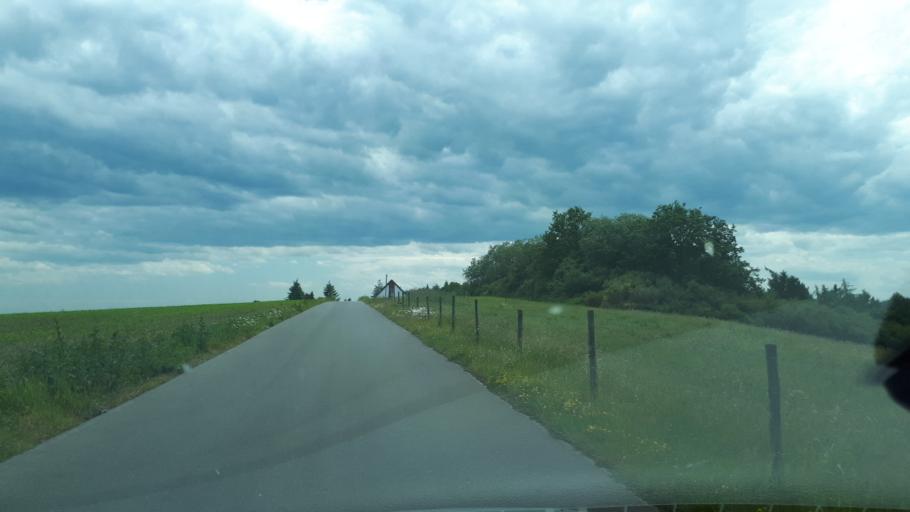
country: DE
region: Rheinland-Pfalz
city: Ellscheid
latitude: 50.1375
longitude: 6.9259
